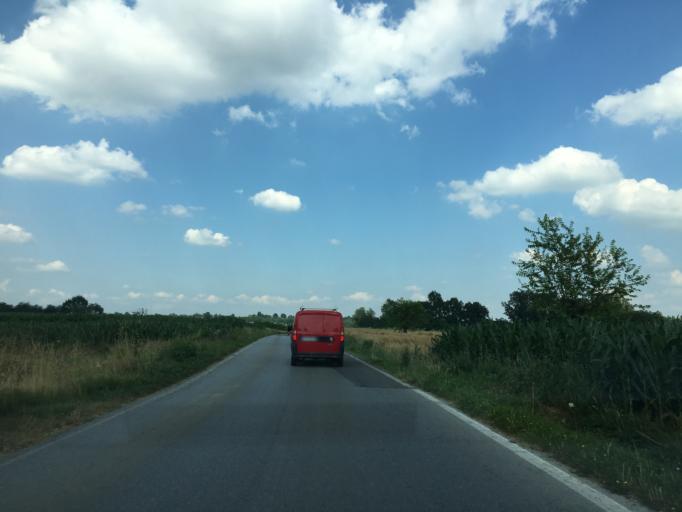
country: IT
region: Piedmont
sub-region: Provincia di Cuneo
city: Ceresole Alba
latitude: 44.7845
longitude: 7.8147
